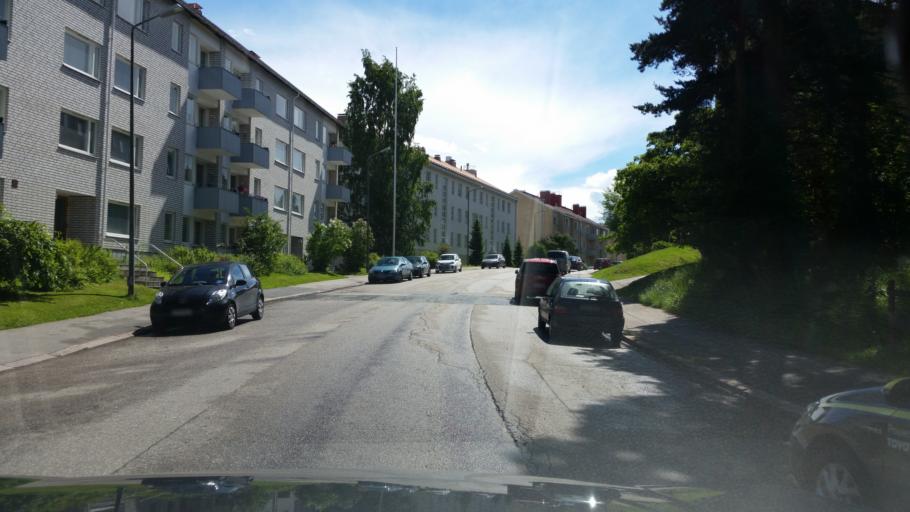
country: FI
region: Uusimaa
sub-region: Helsinki
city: Helsinki
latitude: 60.2022
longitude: 24.9024
